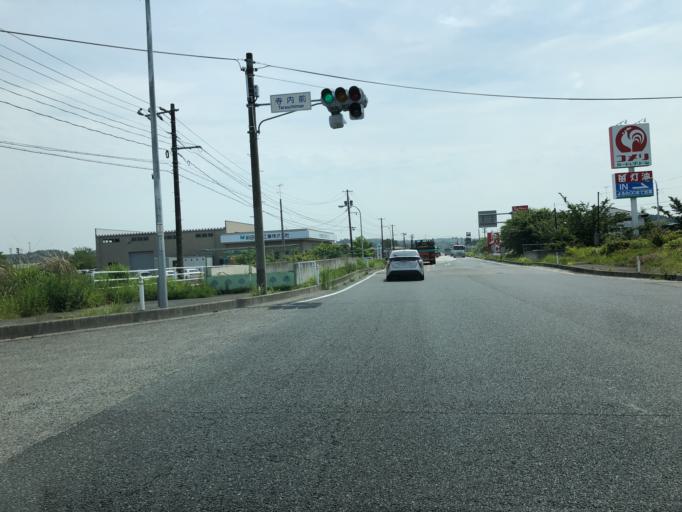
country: JP
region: Fukushima
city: Namie
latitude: 37.4580
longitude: 141.0105
